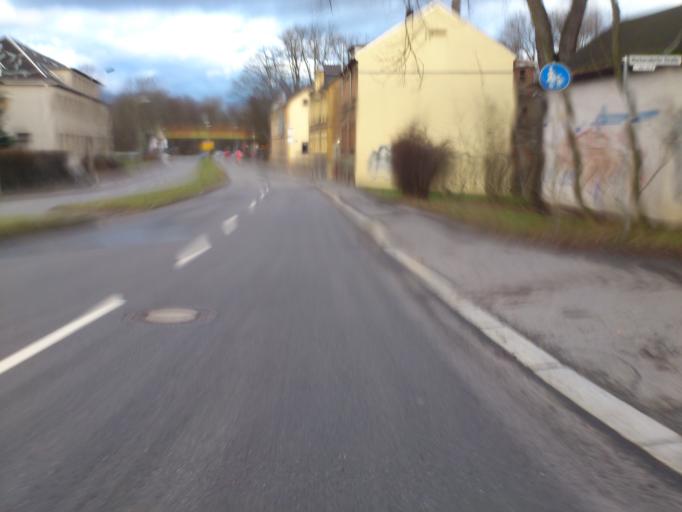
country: DE
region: Saxony
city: Neukirchen
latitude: 50.7944
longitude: 12.9081
